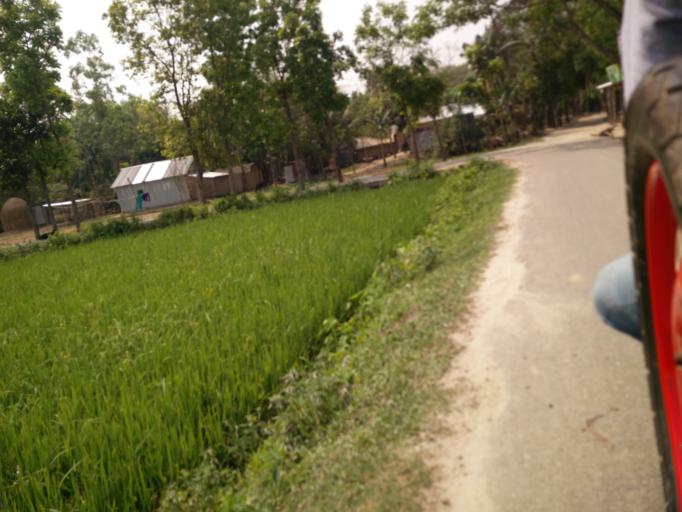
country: BD
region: Dhaka
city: Muktagacha
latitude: 24.8886
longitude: 90.2691
